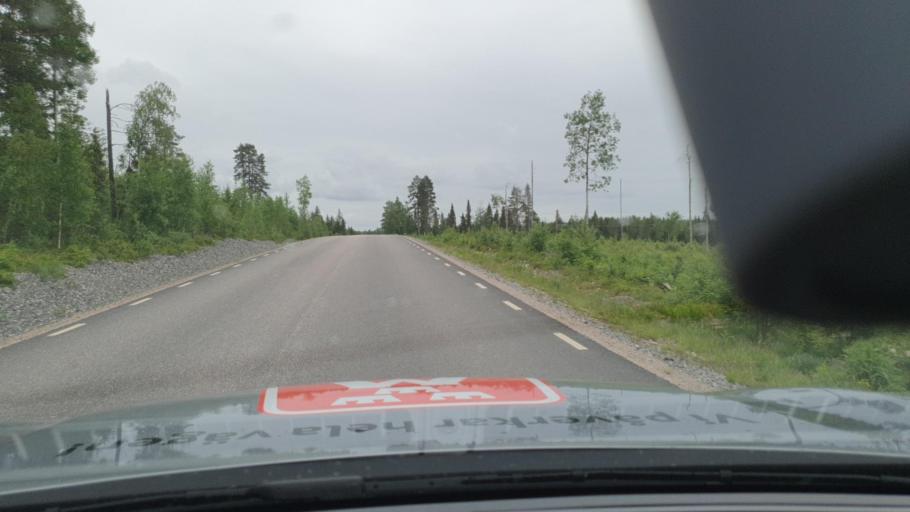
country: SE
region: Norrbotten
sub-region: Overtornea Kommun
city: OEvertornea
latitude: 66.5825
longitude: 23.3277
